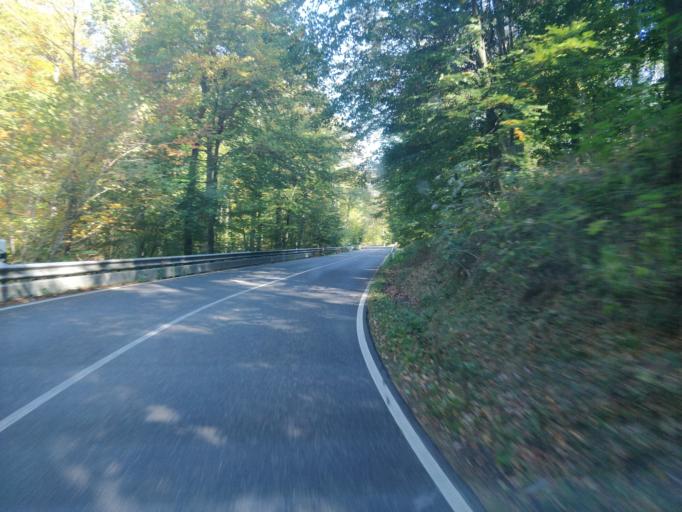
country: DE
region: North Rhine-Westphalia
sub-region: Regierungsbezirk Koln
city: Bad Munstereifel
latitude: 50.5481
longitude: 6.8118
